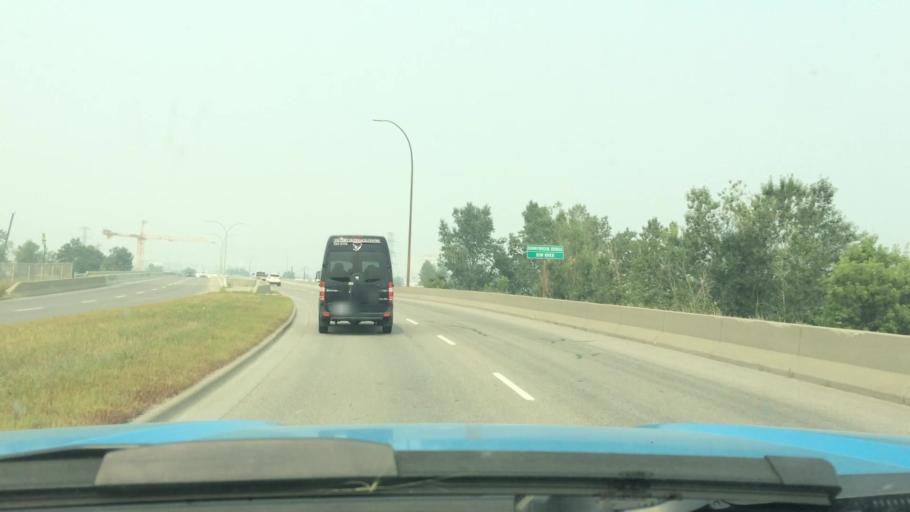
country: CA
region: Alberta
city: Calgary
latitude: 51.0119
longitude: -114.0112
